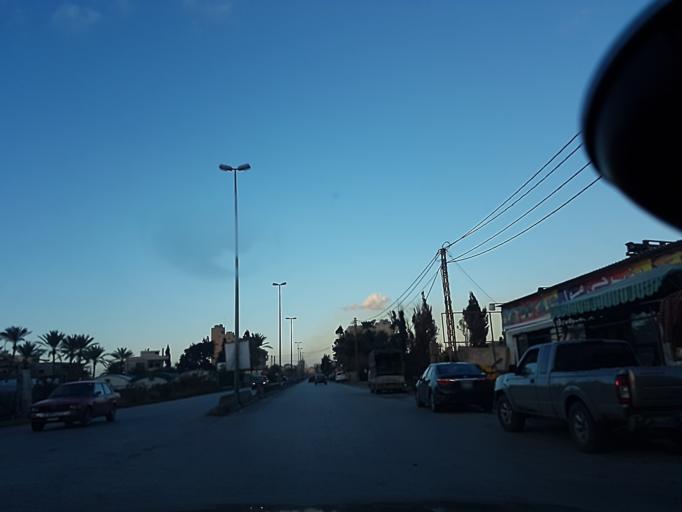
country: LB
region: Liban-Sud
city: Sidon
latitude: 33.5414
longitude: 35.3653
